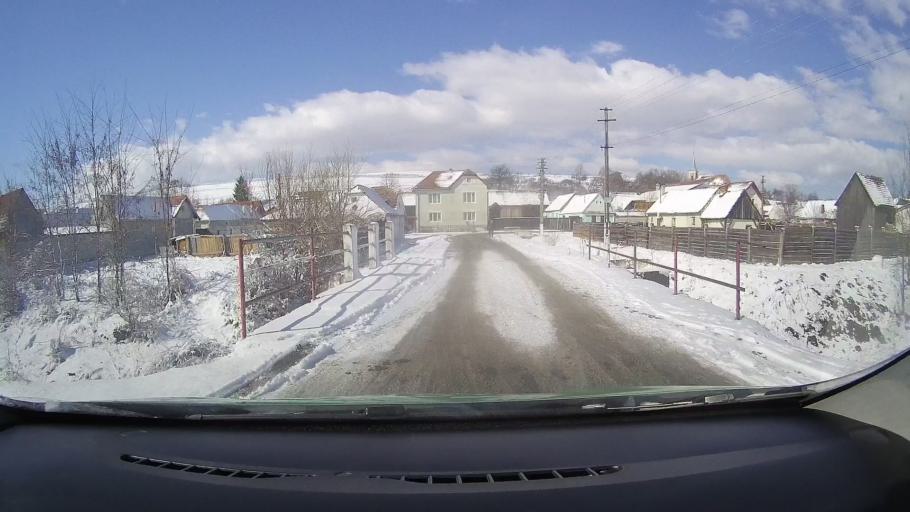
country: RO
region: Sibiu
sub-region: Comuna Vurpar
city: Vurpar
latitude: 45.8923
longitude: 24.3382
